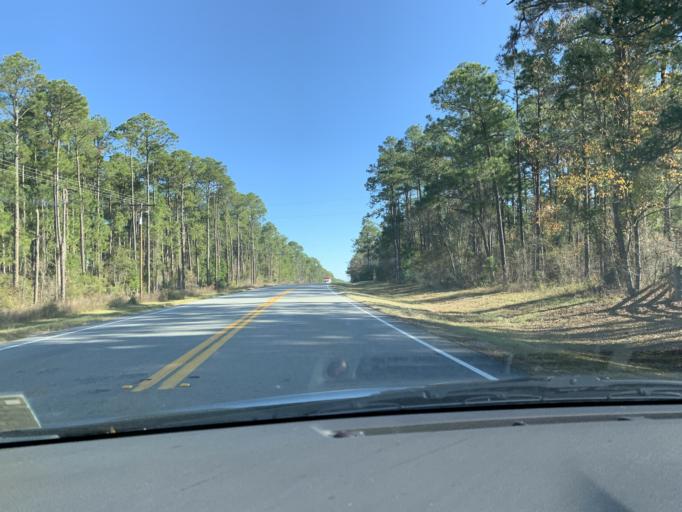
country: US
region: Georgia
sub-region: Ben Hill County
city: Fitzgerald
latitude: 31.7294
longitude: -83.1758
